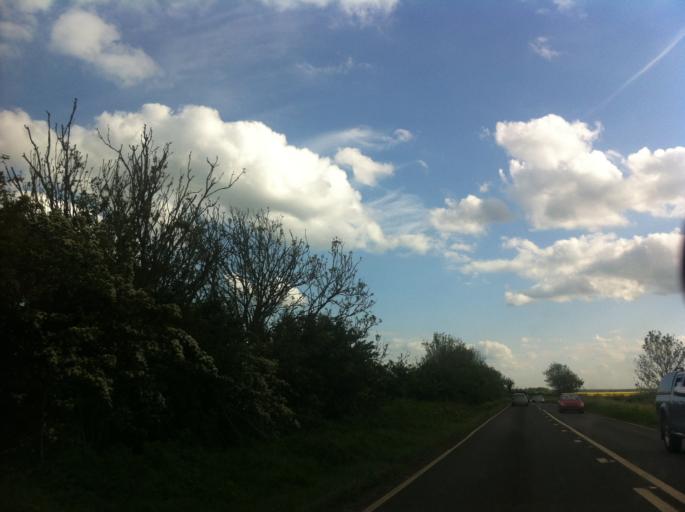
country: GB
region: England
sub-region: Northamptonshire
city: Irchester
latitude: 52.2674
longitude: -0.6771
